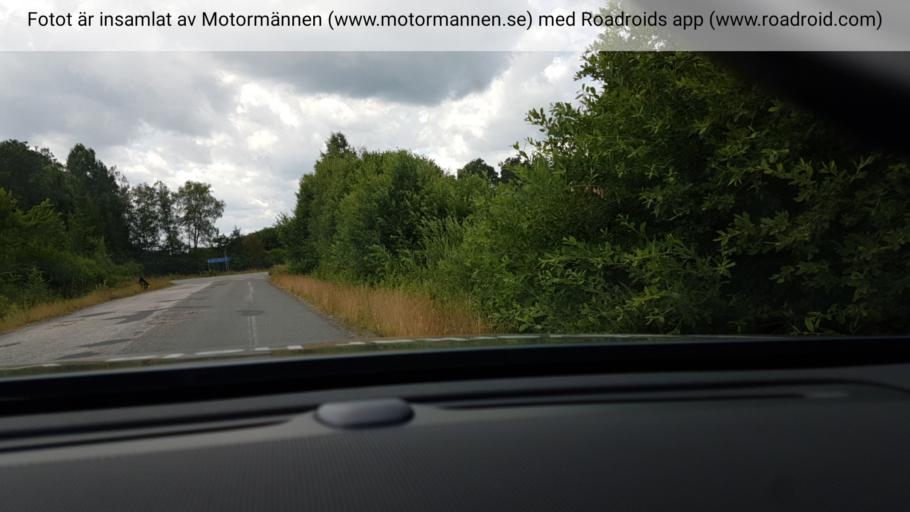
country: SE
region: Skane
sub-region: Hassleholms Kommun
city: Hassleholm
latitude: 56.2188
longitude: 13.8459
